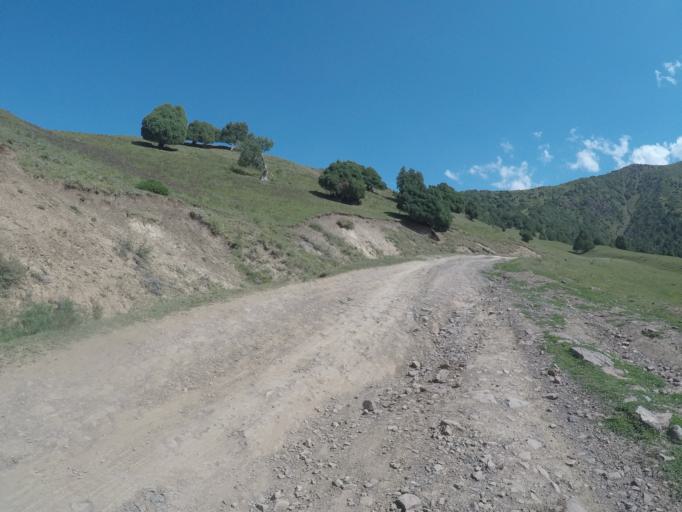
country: KG
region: Chuy
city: Bishkek
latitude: 42.6481
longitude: 74.5546
